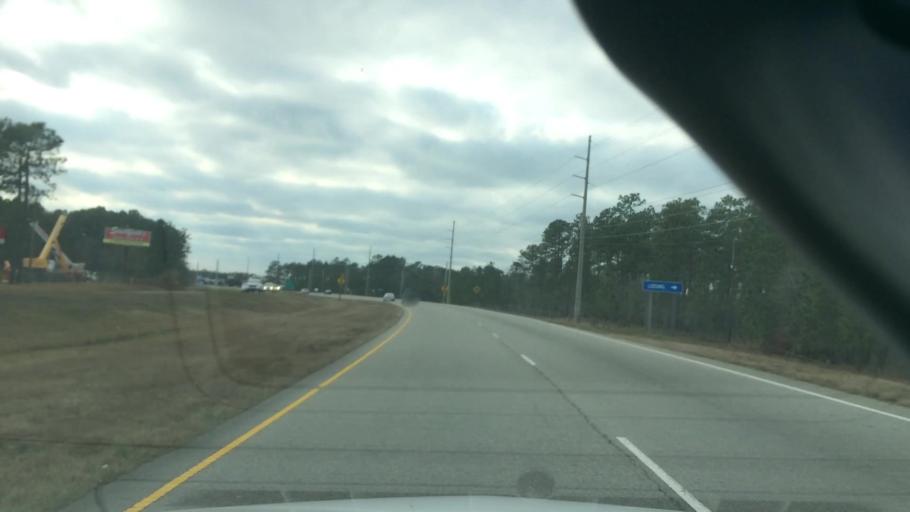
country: US
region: North Carolina
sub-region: Brunswick County
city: Shallotte
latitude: 33.9891
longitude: -78.3870
